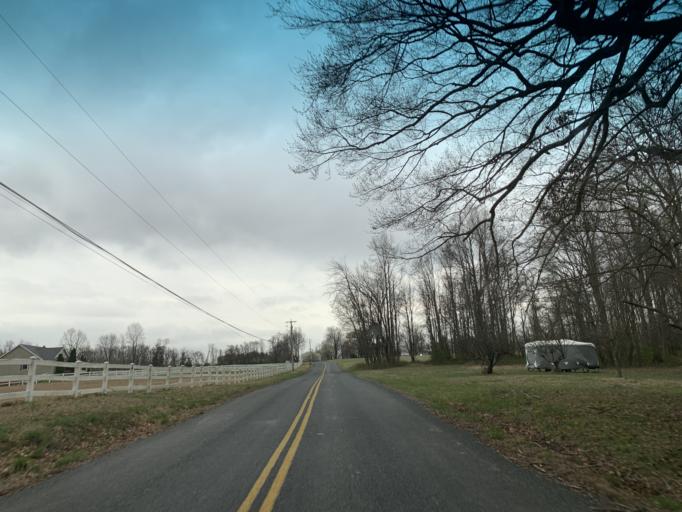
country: US
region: Maryland
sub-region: Harford County
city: Aberdeen
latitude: 39.5288
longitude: -76.2088
